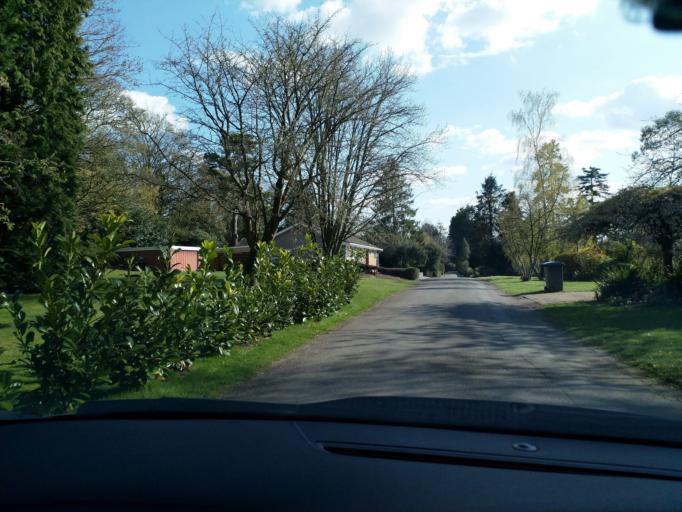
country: GB
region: England
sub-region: Warwickshire
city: Wellesbourne Mountford
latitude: 52.1899
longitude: -1.5543
